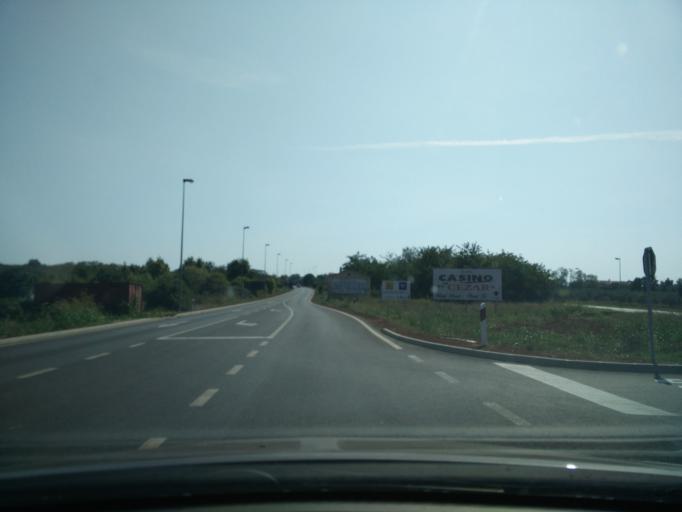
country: HR
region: Istarska
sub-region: Grad Porec
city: Porec
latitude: 45.2564
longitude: 13.6114
